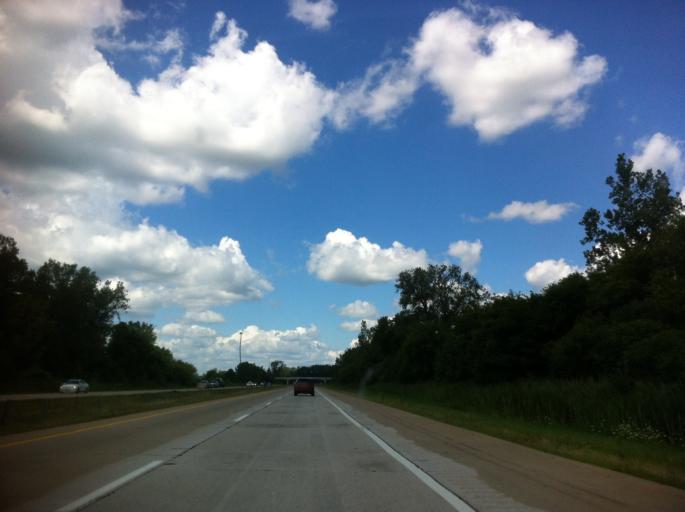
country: US
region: Michigan
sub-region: Monroe County
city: Lambertville
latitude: 41.8162
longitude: -83.6840
